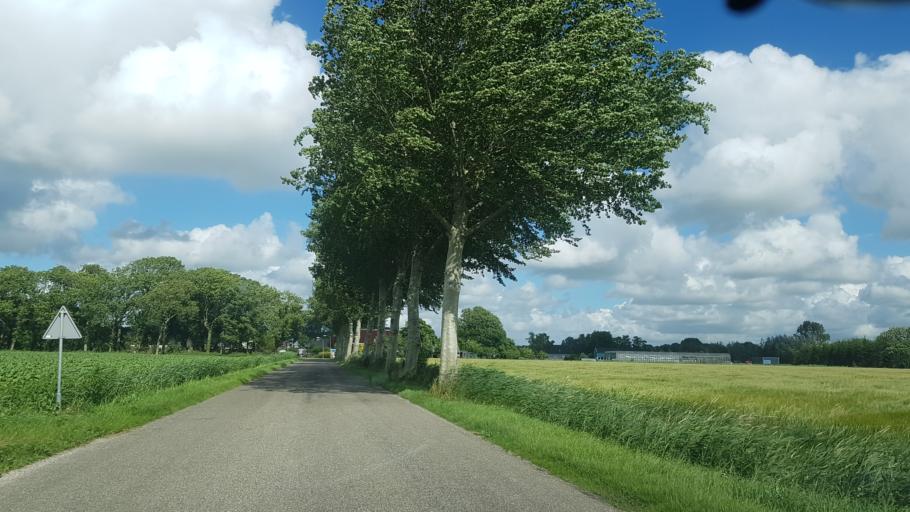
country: NL
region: Groningen
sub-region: Gemeente Bedum
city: Bedum
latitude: 53.4088
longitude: 6.6488
